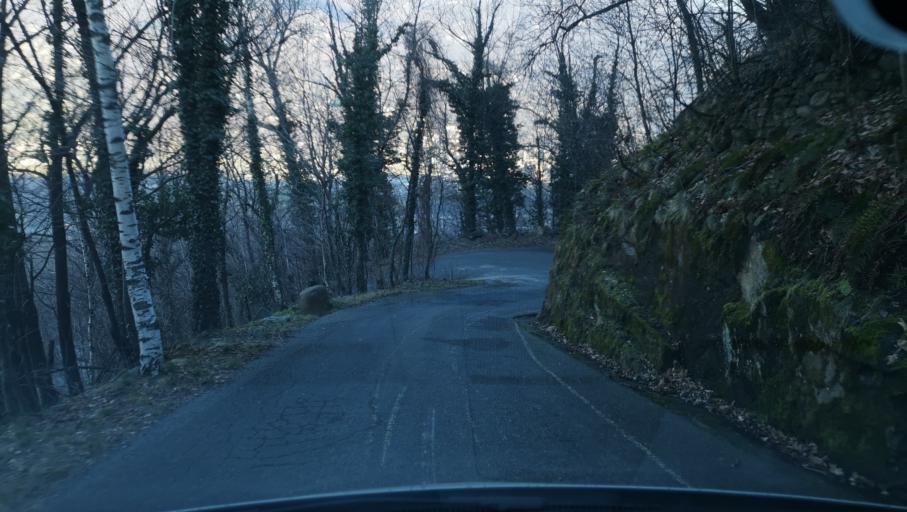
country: IT
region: Piedmont
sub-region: Provincia di Torino
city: Tavagnasco
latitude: 45.5472
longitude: 7.8129
